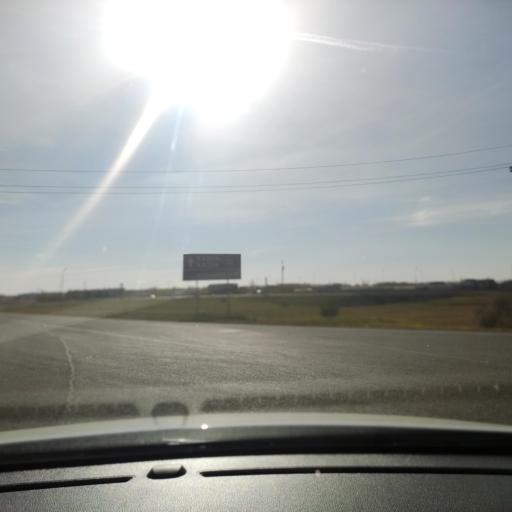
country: RU
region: Tatarstan
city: Vysokaya Gora
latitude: 55.7474
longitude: 49.4006
